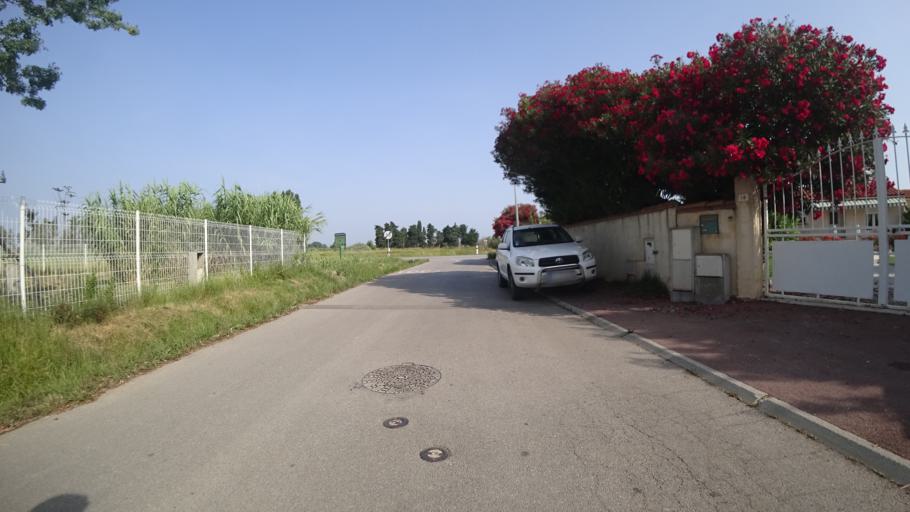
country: FR
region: Languedoc-Roussillon
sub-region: Departement des Pyrenees-Orientales
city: Sainte-Marie-Plage
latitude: 42.7304
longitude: 3.0130
